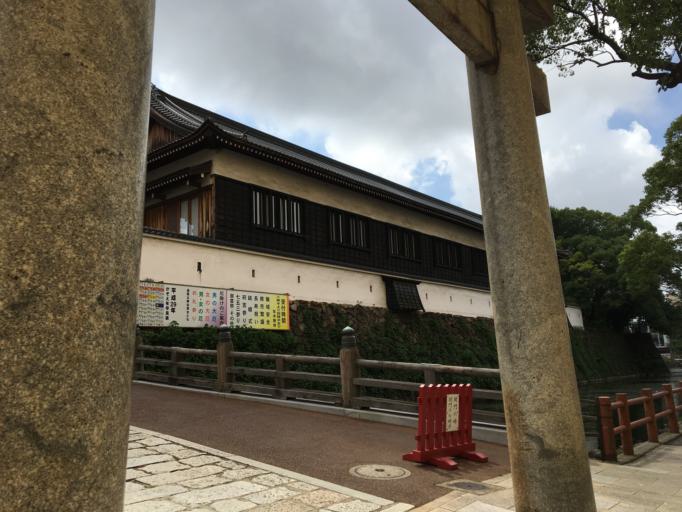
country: JP
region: Fukuoka
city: Kitakyushu
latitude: 33.8858
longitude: 130.8740
